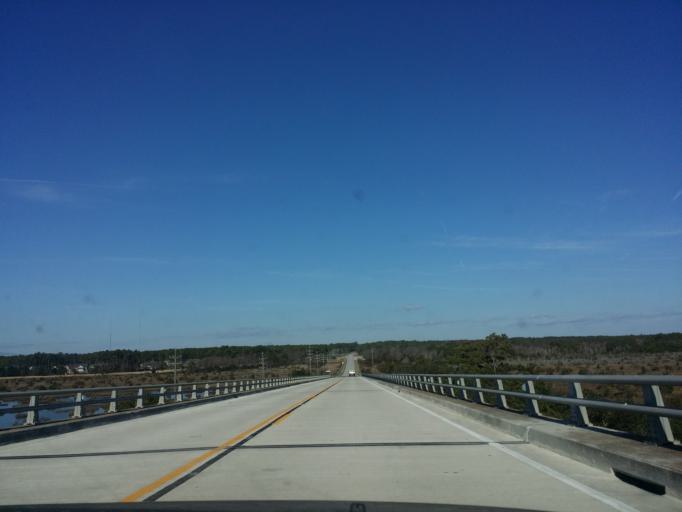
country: US
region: North Carolina
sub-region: Onslow County
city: Sneads Ferry
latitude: 34.5014
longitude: -77.4300
